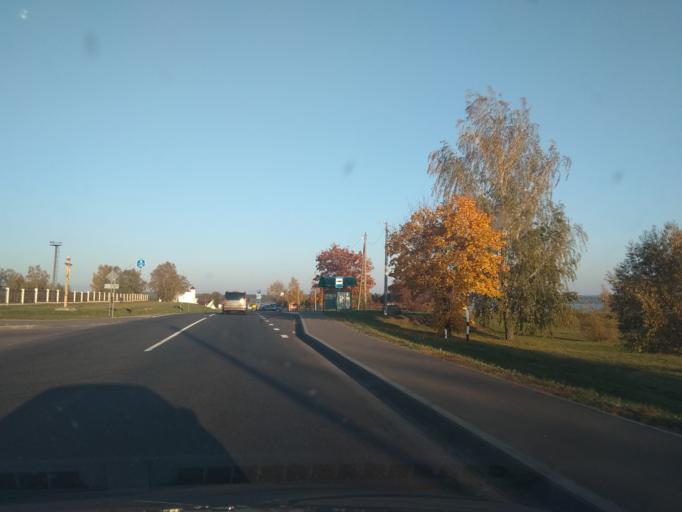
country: BY
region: Grodnenskaya
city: Zel'va
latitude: 53.1432
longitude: 24.8198
